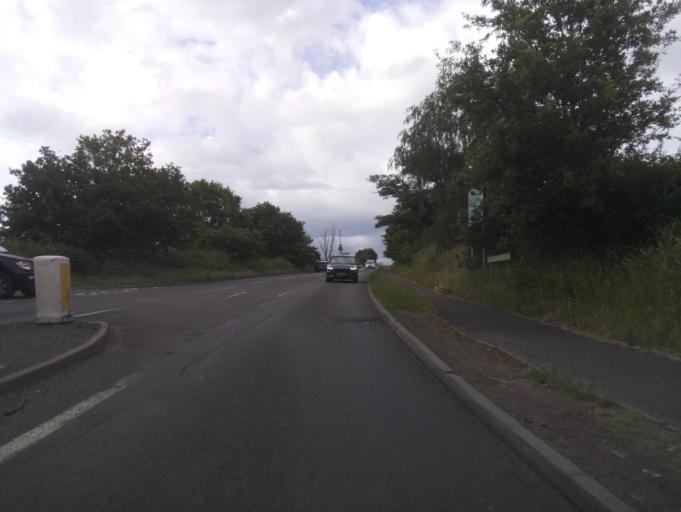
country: GB
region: England
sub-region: Dudley
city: Kingswinford
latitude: 52.4892
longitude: -2.1898
